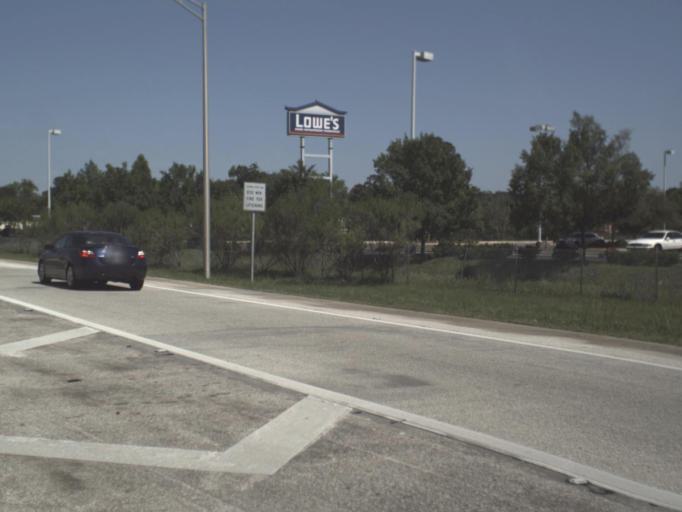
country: US
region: Florida
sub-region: Duval County
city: Jacksonville
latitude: 30.3171
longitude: -81.7333
